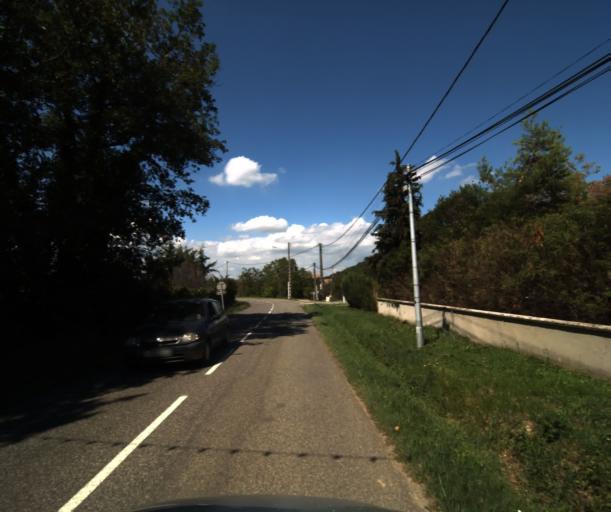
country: FR
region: Midi-Pyrenees
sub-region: Departement de la Haute-Garonne
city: Le Fauga
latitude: 43.4161
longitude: 1.3145
